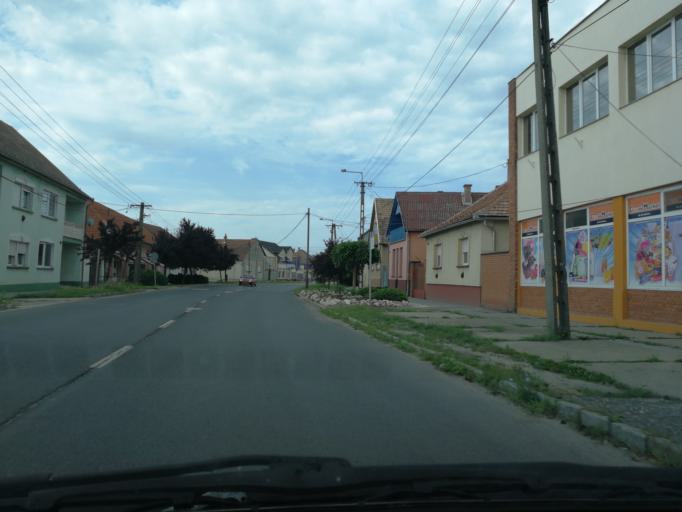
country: HU
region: Bacs-Kiskun
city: Baja
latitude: 46.2021
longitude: 18.9587
